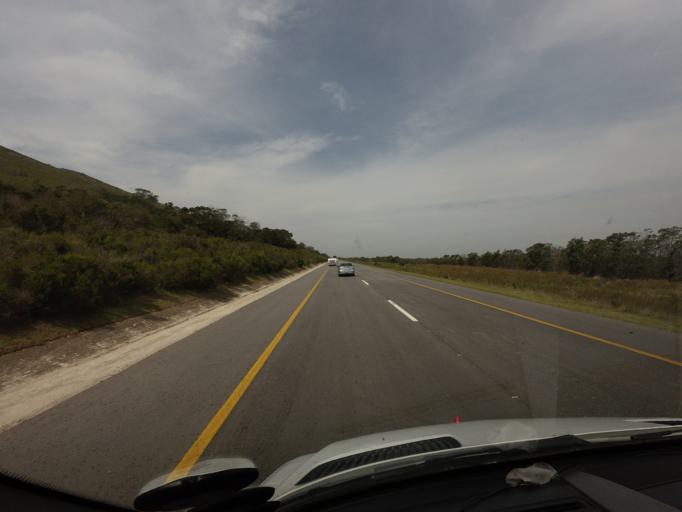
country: ZA
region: Eastern Cape
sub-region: Cacadu District Municipality
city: Kruisfontein
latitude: -33.9948
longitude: 24.7217
